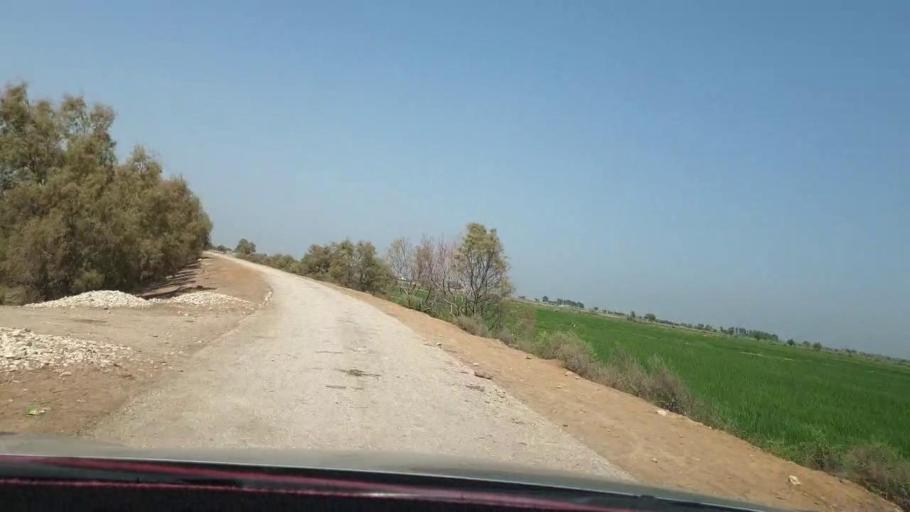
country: PK
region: Sindh
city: Warah
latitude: 27.5182
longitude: 67.7085
